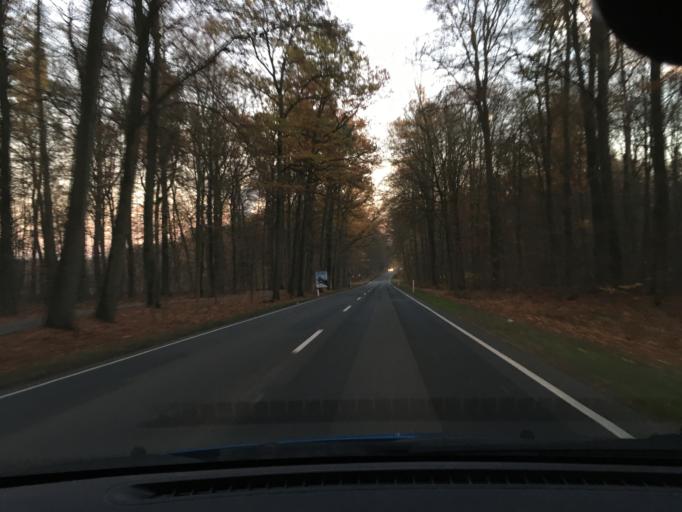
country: DE
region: Lower Saxony
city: Uelzen
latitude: 52.9792
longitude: 10.5351
